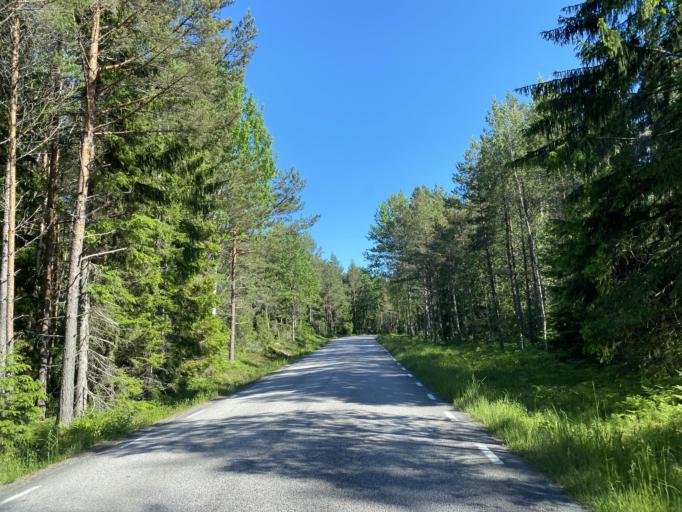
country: SE
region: Stockholm
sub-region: Norrtalje Kommun
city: Bjorko
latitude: 59.8867
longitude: 18.9782
